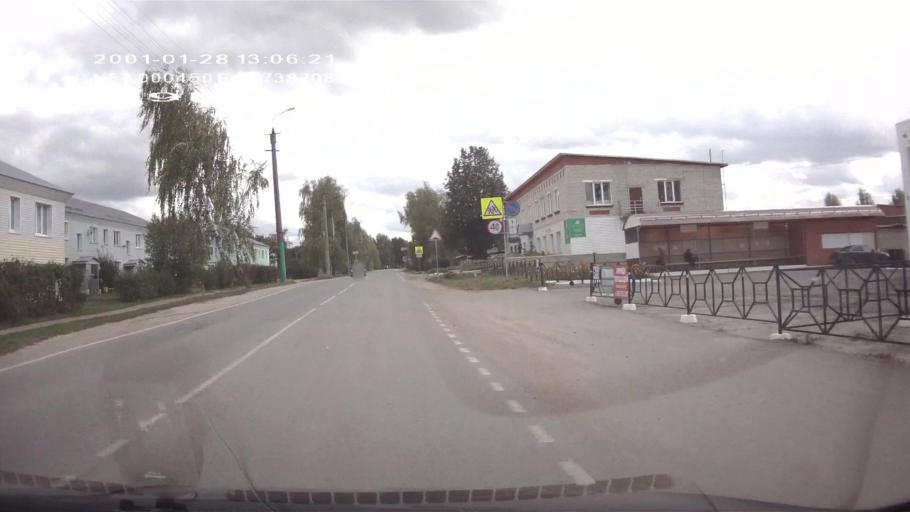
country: RU
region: Mariy-El
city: Kuzhener
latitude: 57.0001
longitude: 48.7390
